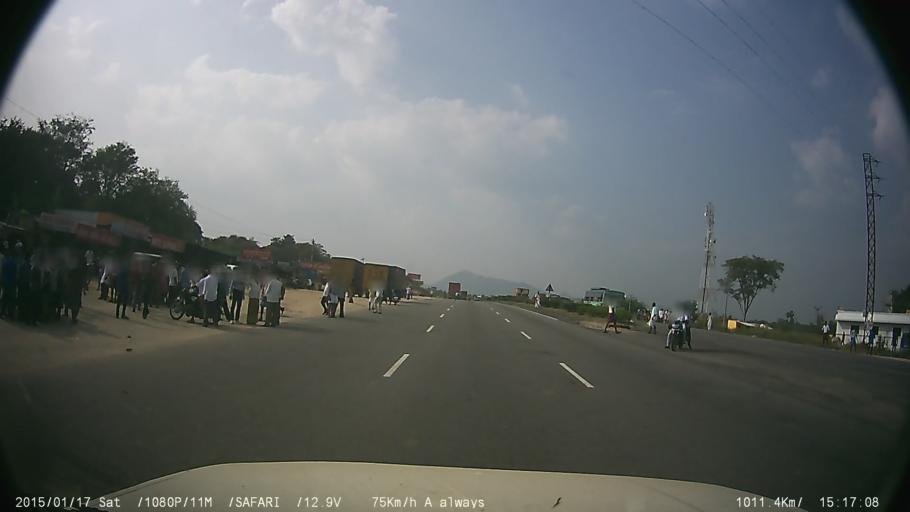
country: IN
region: Tamil Nadu
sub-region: Krishnagiri
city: Krishnagiri
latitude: 12.5795
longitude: 78.1619
